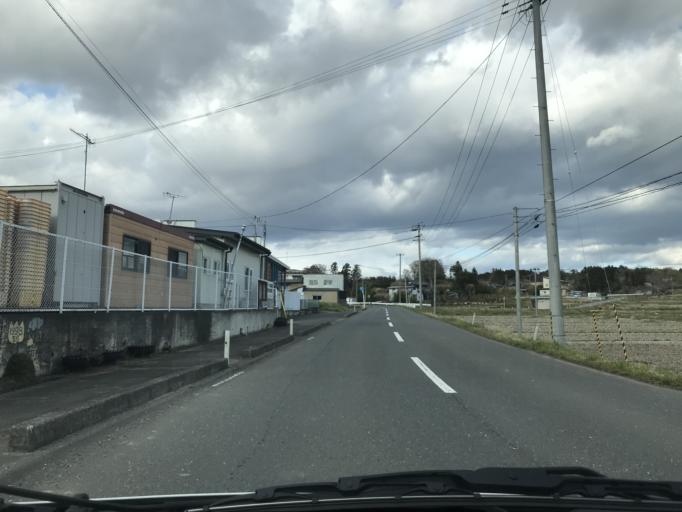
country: JP
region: Miyagi
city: Wakuya
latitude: 38.6323
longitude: 141.2130
